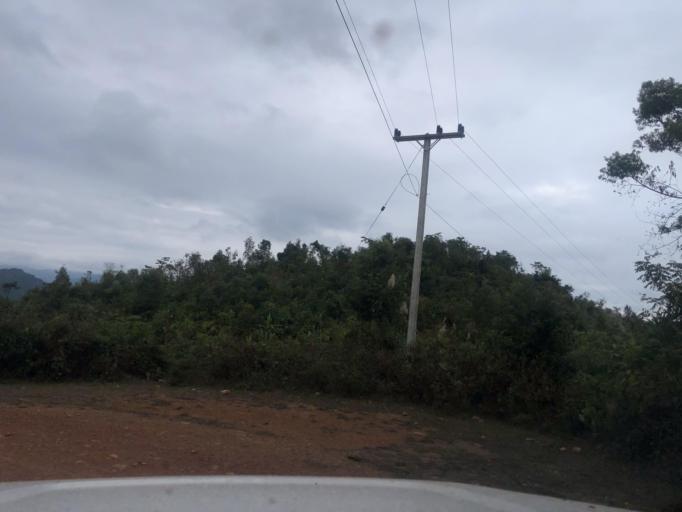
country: LA
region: Phongsali
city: Khoa
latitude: 21.2720
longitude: 102.5833
